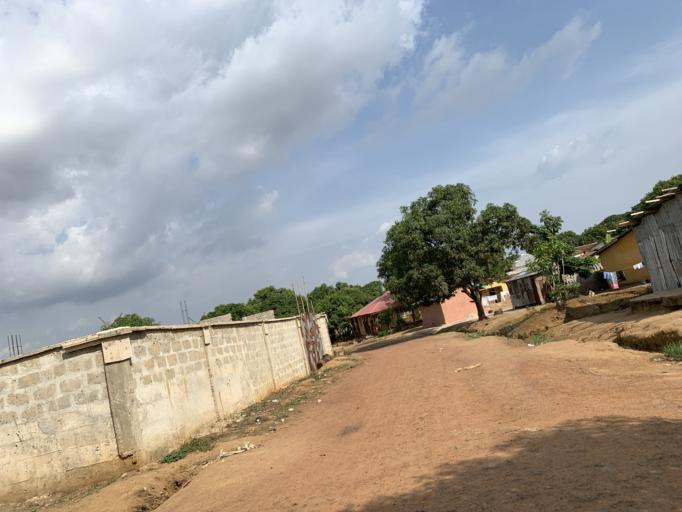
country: SL
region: Western Area
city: Waterloo
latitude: 8.3409
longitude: -13.0460
